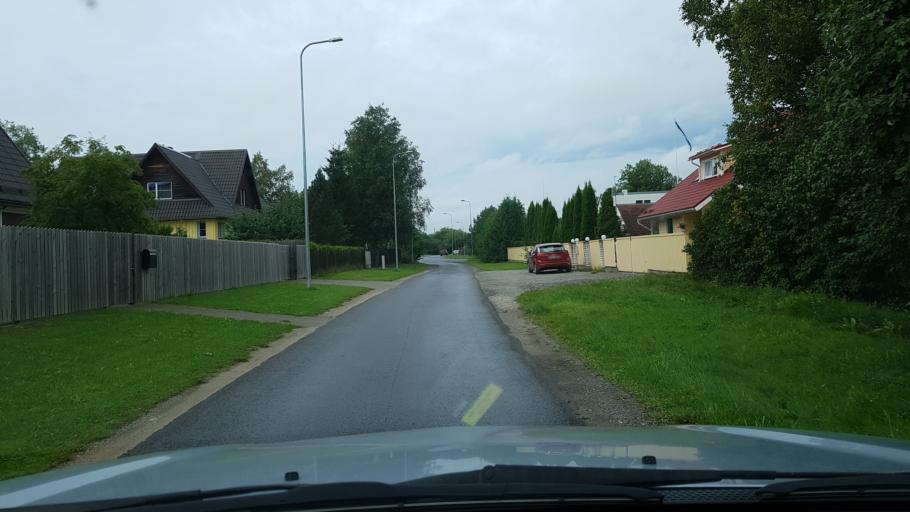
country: EE
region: Harju
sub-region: Rae vald
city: Jueri
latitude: 59.3548
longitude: 24.9196
